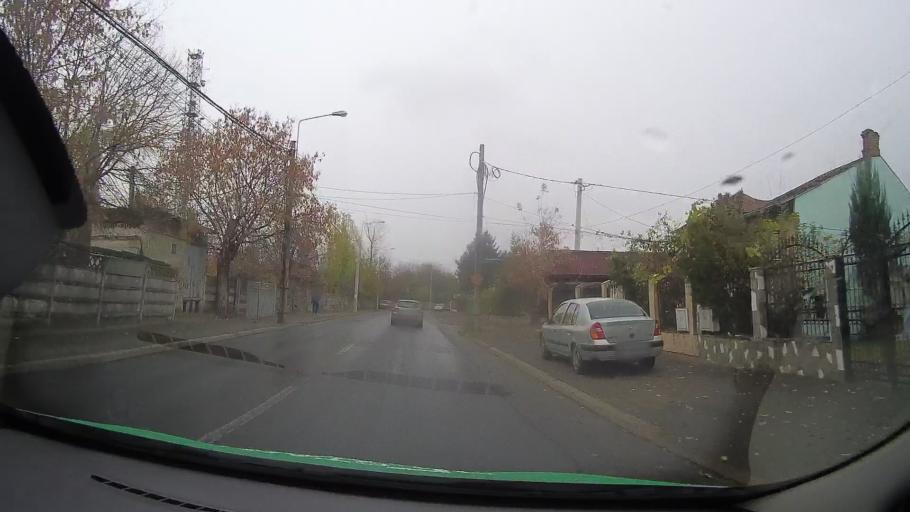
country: RO
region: Prahova
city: Ploiesti
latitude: 44.9351
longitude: 26.0051
